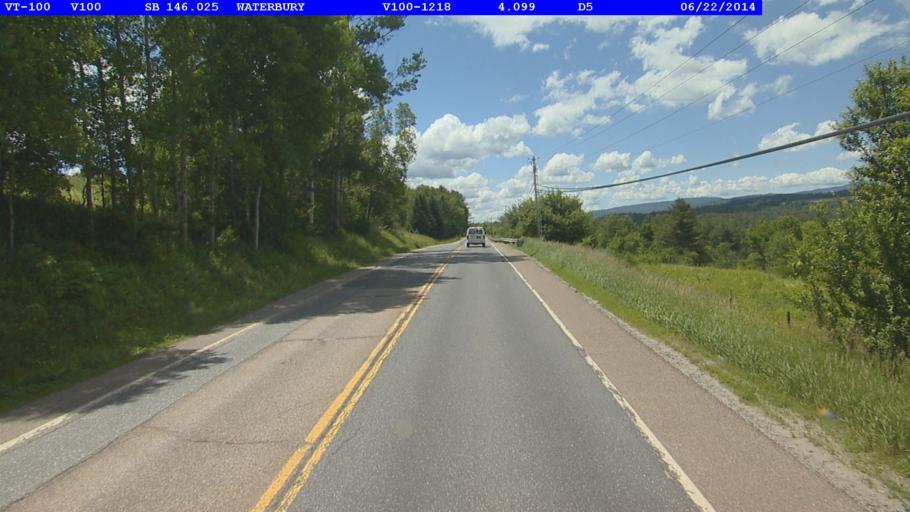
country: US
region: Vermont
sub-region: Washington County
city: Waterbury
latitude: 44.3880
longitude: -72.7193
